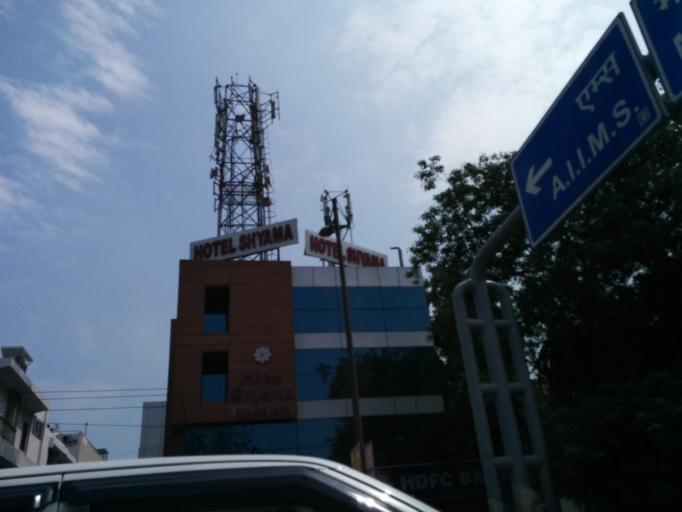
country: IN
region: NCT
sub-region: New Delhi
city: New Delhi
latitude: 28.5458
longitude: 77.1977
